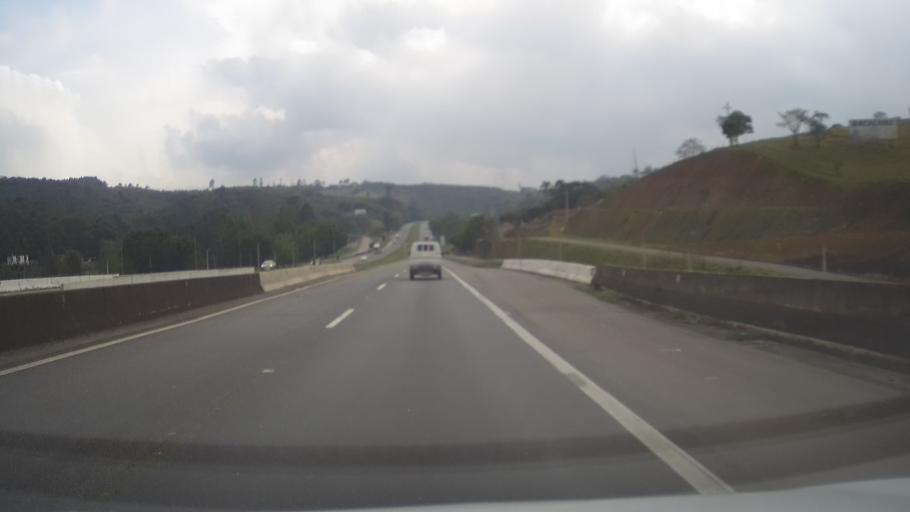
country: BR
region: Minas Gerais
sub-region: Extrema
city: Extrema
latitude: -22.8826
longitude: -46.4074
